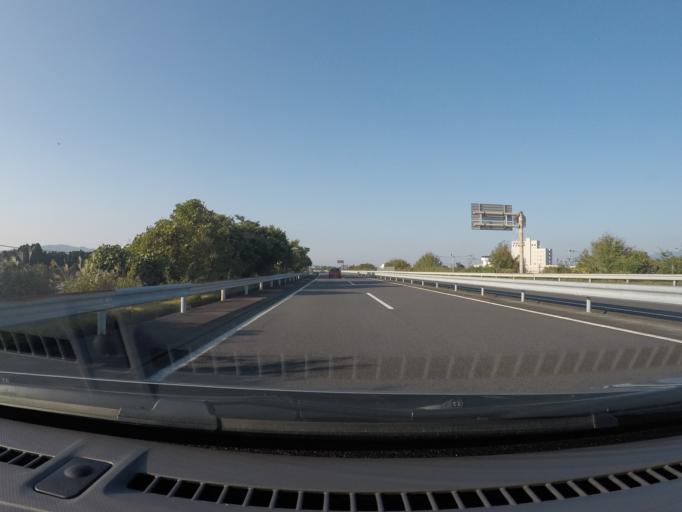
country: JP
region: Kagoshima
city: Kokubu-matsuki
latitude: 31.7924
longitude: 130.7168
